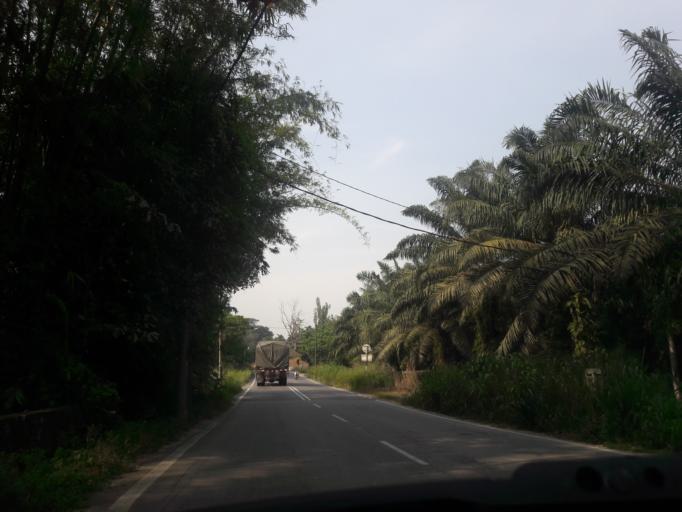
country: MY
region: Kedah
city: Kulim
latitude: 5.3599
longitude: 100.5210
